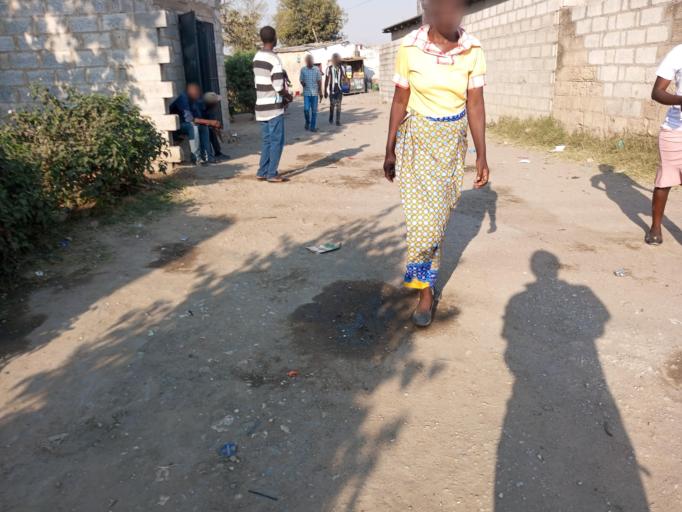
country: ZM
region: Lusaka
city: Lusaka
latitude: -15.3903
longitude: 28.2872
